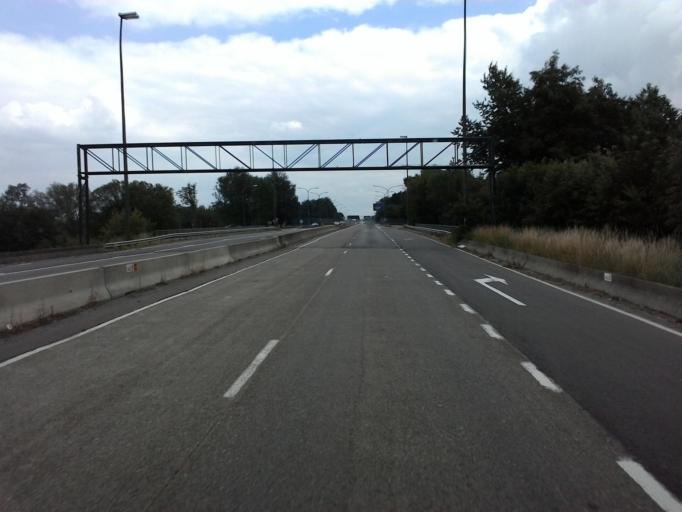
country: BE
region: Wallonia
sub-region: Province du Luxembourg
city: Bastogne
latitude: 49.9959
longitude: 5.7012
